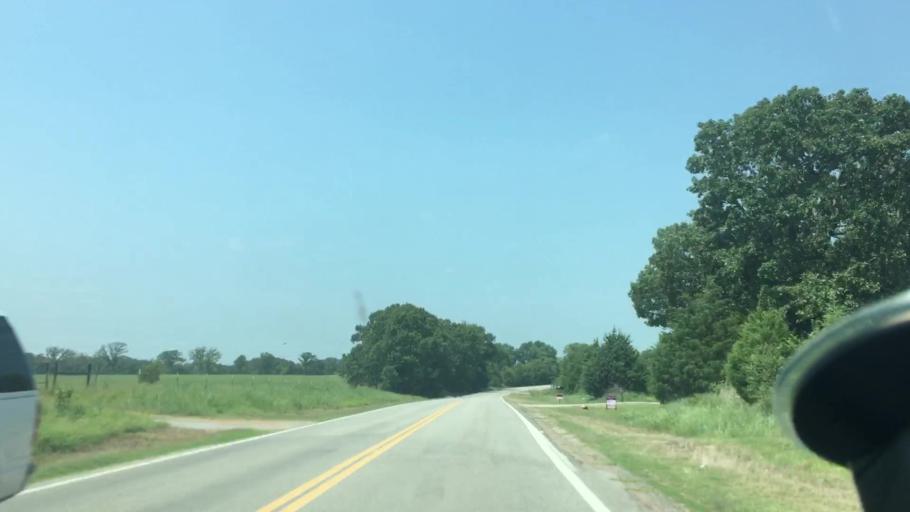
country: US
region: Oklahoma
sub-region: Atoka County
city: Atoka
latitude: 34.2800
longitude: -95.9466
